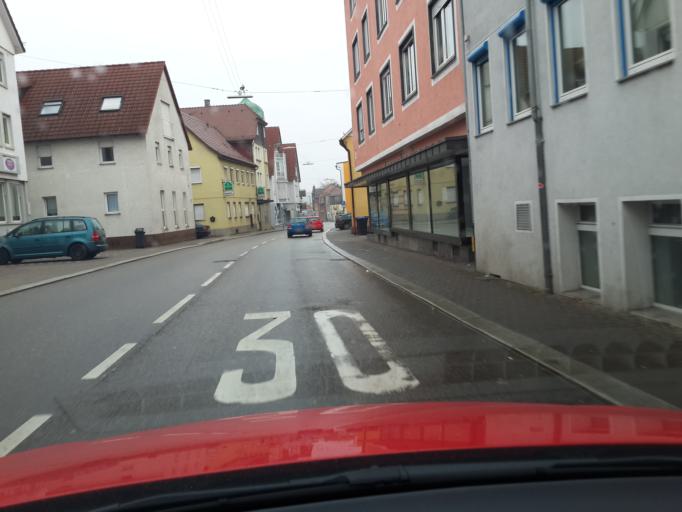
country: DE
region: Baden-Wuerttemberg
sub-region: Regierungsbezirk Stuttgart
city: Neckarsulm
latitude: 49.1689
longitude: 9.2003
